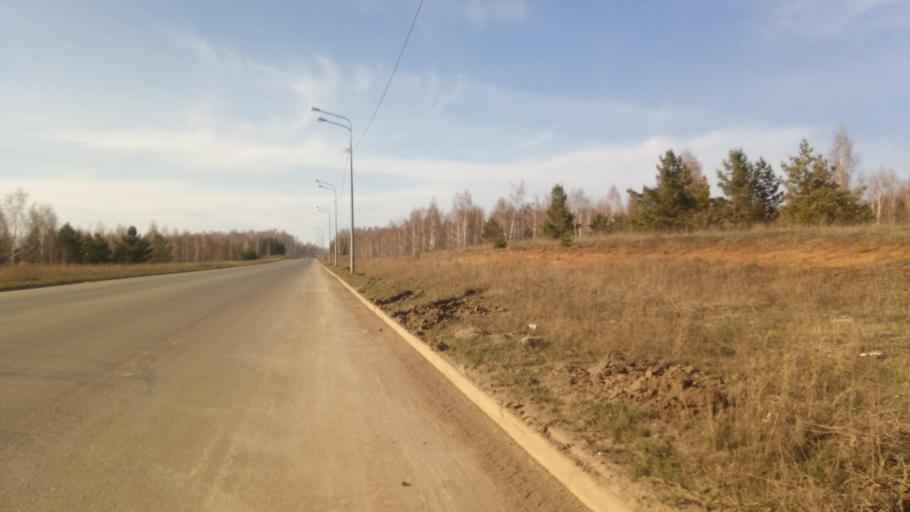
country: RU
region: Chelyabinsk
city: Sargazy
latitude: 55.1153
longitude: 61.2548
